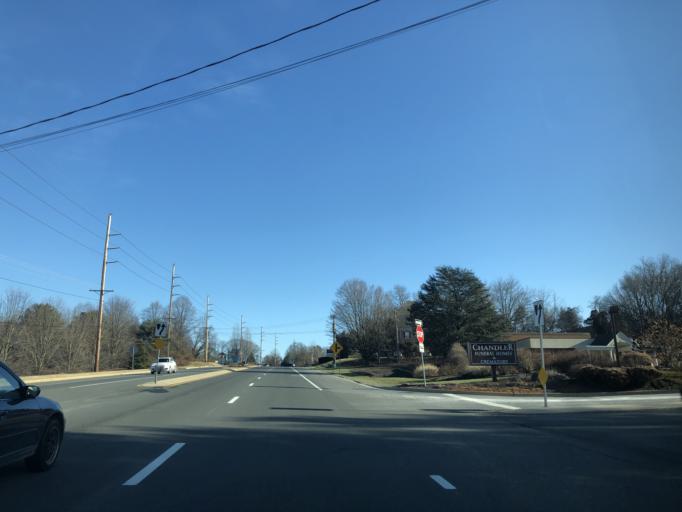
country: US
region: Delaware
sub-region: New Castle County
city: Hockessin
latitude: 39.7867
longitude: -75.6892
